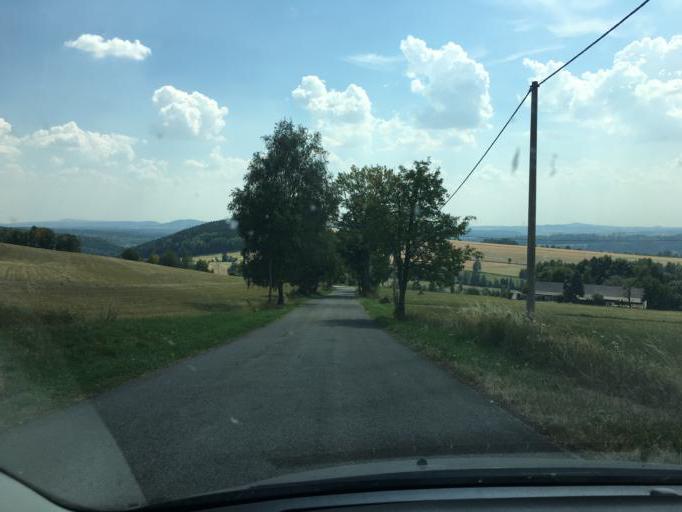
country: CZ
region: Liberecky
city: Jilemnice
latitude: 50.6454
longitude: 15.5030
